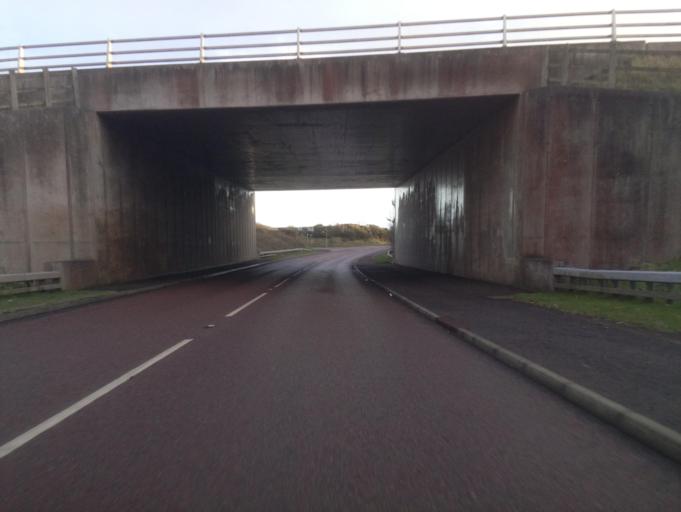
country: GB
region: Scotland
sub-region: Fife
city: Tayport
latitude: 56.4990
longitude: -2.8052
